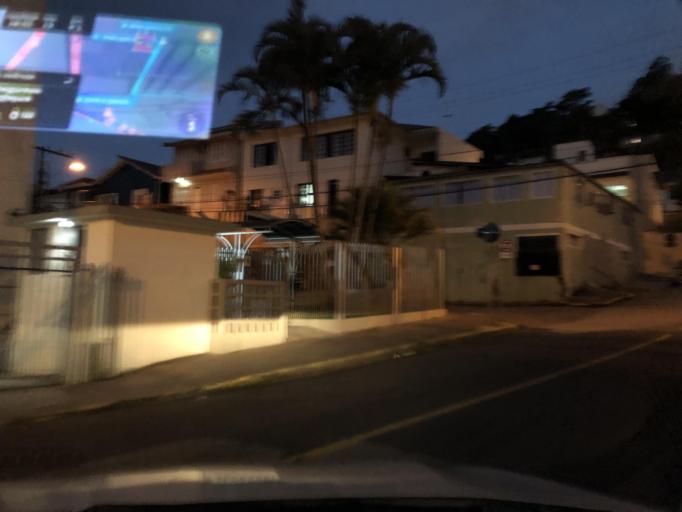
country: BR
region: Santa Catarina
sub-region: Florianopolis
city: Morro da Cruz
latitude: -27.5869
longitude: -48.5421
